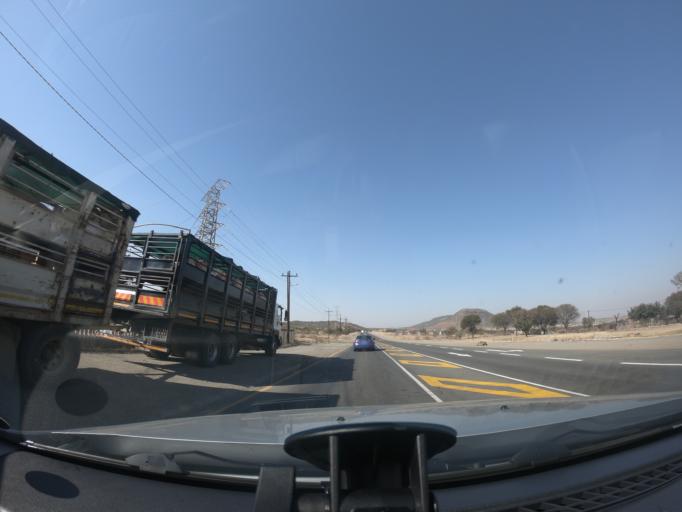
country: ZA
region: KwaZulu-Natal
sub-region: uThukela District Municipality
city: Ladysmith
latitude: -28.5512
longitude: 29.8319
